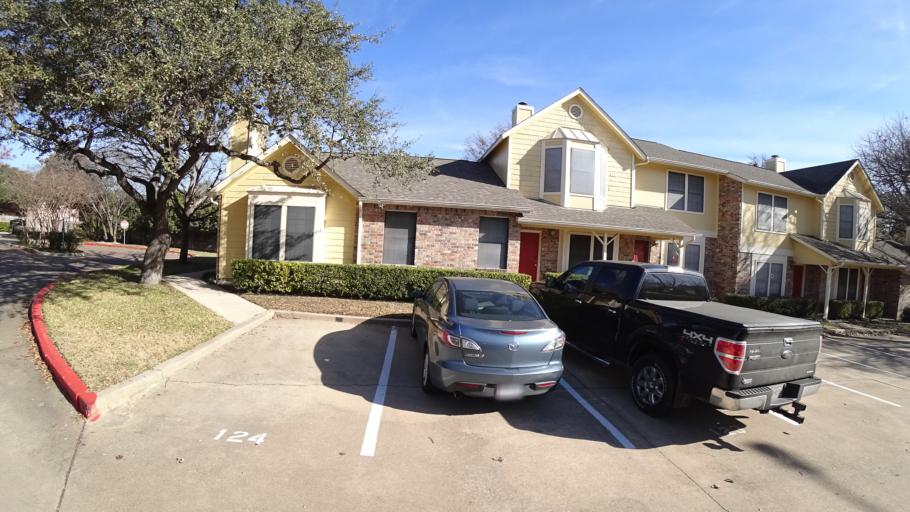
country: US
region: Texas
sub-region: Travis County
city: Wells Branch
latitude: 30.3953
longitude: -97.6924
